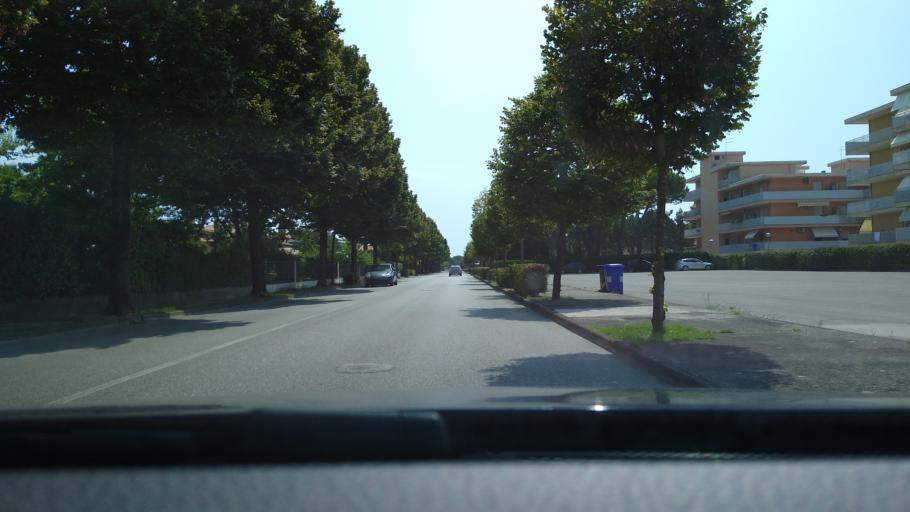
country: IT
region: Veneto
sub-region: Provincia di Venezia
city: Bibione
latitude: 45.6483
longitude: 13.0545
